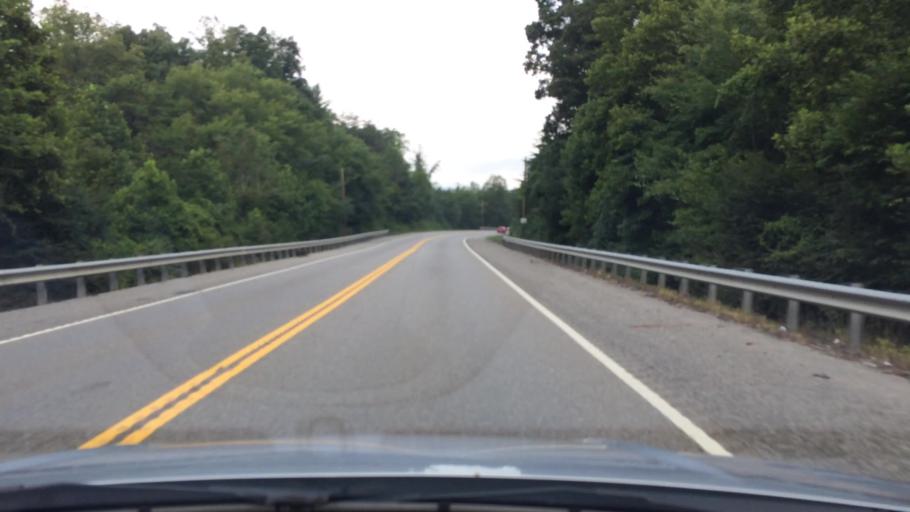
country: US
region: Tennessee
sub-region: Campbell County
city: Jacksboro
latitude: 36.3905
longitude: -84.2604
